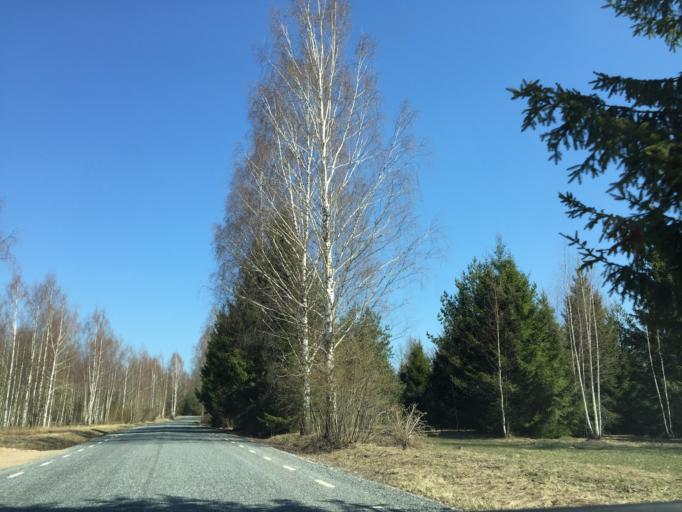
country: EE
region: Tartu
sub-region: Alatskivi vald
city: Kallaste
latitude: 58.5896
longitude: 27.0622
